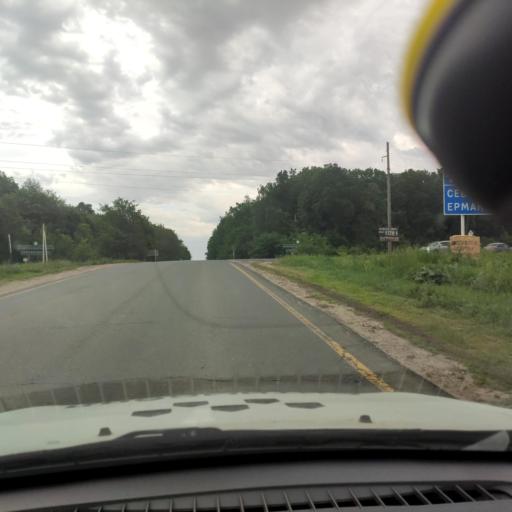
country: RU
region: Samara
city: Zhigulevsk
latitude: 53.3398
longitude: 49.4834
